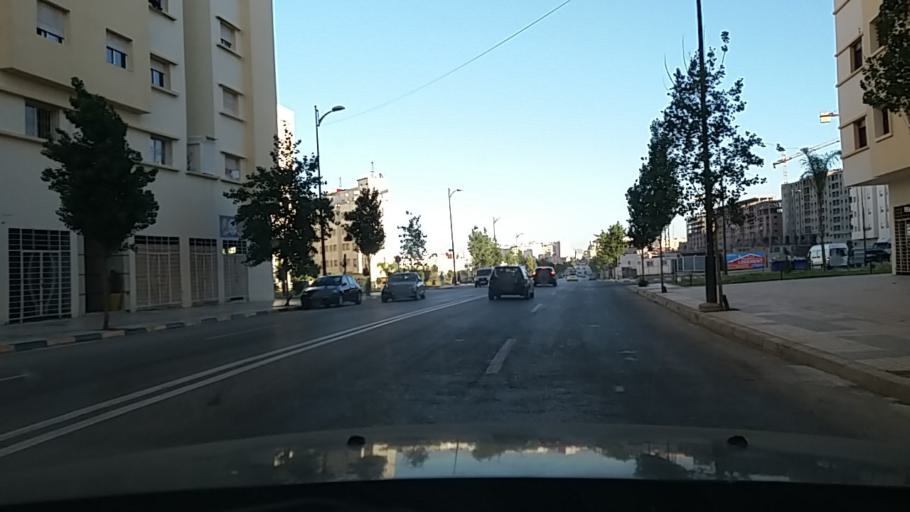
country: MA
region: Tanger-Tetouan
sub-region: Tanger-Assilah
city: Boukhalef
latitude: 35.7662
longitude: -5.8575
